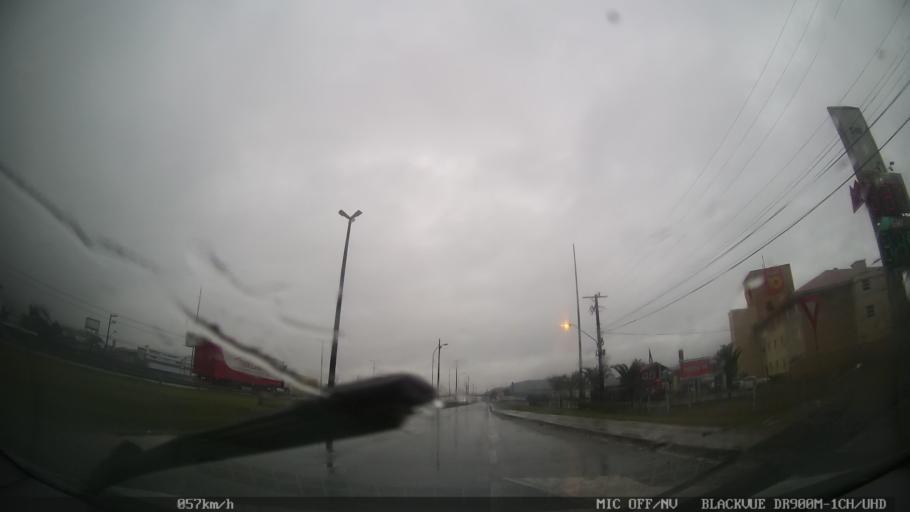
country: BR
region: Santa Catarina
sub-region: Itajai
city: Itajai
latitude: -26.8839
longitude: -48.7242
